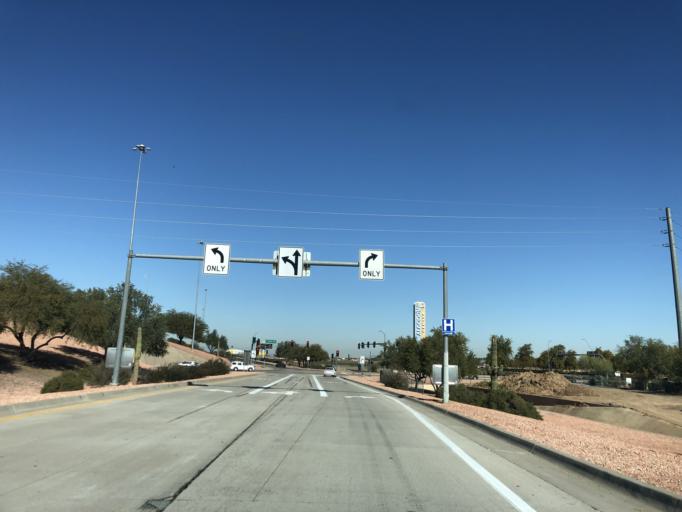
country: US
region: Arizona
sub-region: Maricopa County
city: Tolleson
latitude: 33.4783
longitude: -112.2634
